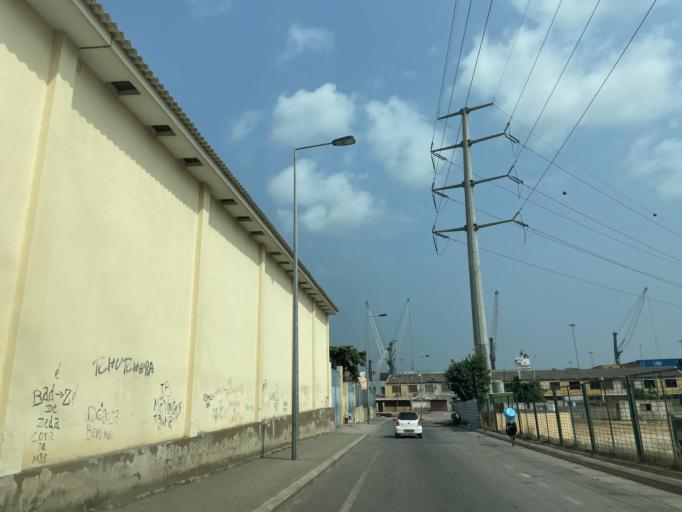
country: AO
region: Luanda
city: Luanda
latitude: -8.8041
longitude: 13.2527
